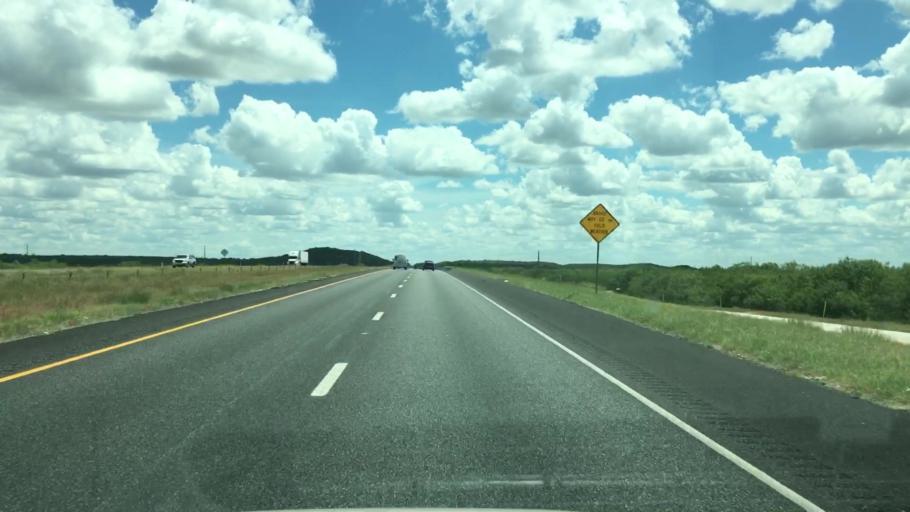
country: US
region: Texas
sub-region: Live Oak County
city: Three Rivers
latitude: 28.7361
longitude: -98.2903
